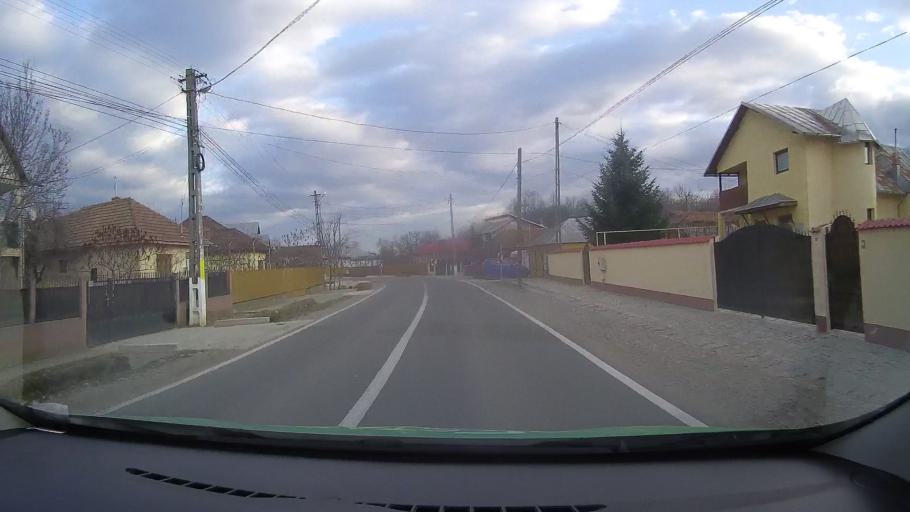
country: RO
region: Dambovita
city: Ion Luca Caragiale
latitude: 44.9149
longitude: 25.6916
